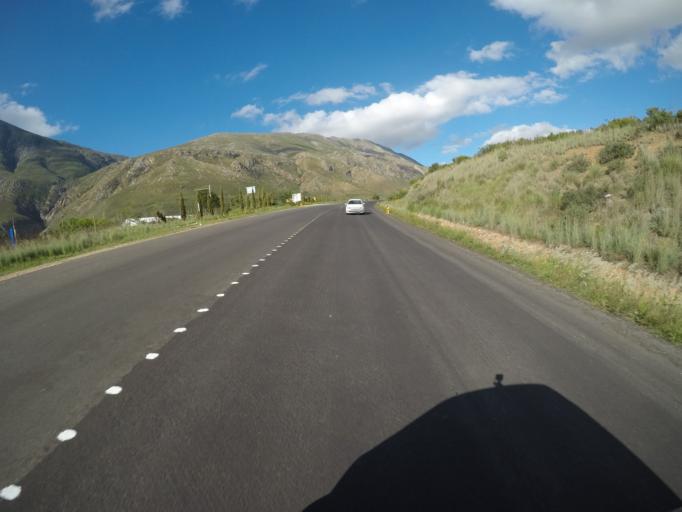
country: ZA
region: Western Cape
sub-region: Cape Winelands District Municipality
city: Ashton
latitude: -33.8733
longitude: 20.1585
